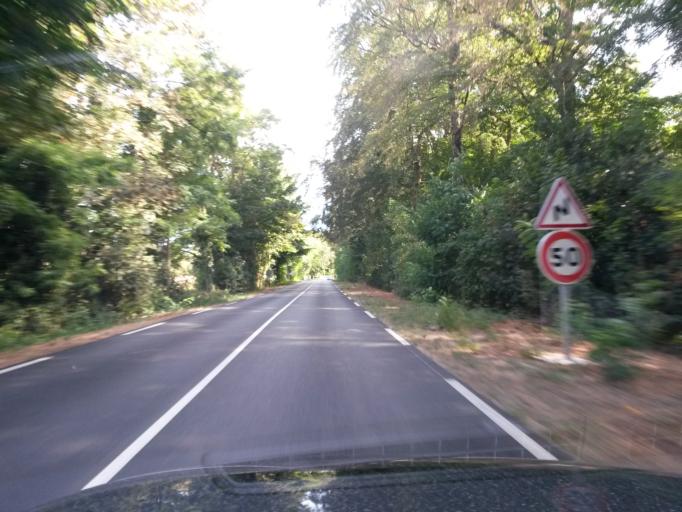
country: FR
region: Pays de la Loire
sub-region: Departement de la Vendee
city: Olonne-sur-Mer
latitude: 46.5603
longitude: -1.8115
